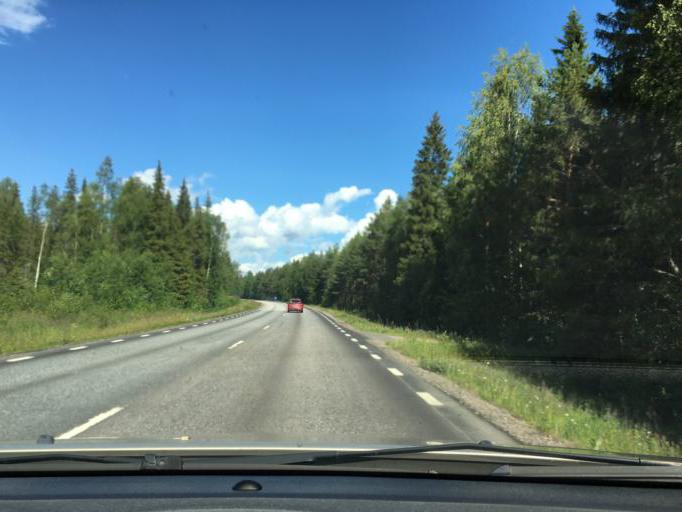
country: SE
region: Norrbotten
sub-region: Overkalix Kommun
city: OEverkalix
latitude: 66.2697
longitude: 22.8189
